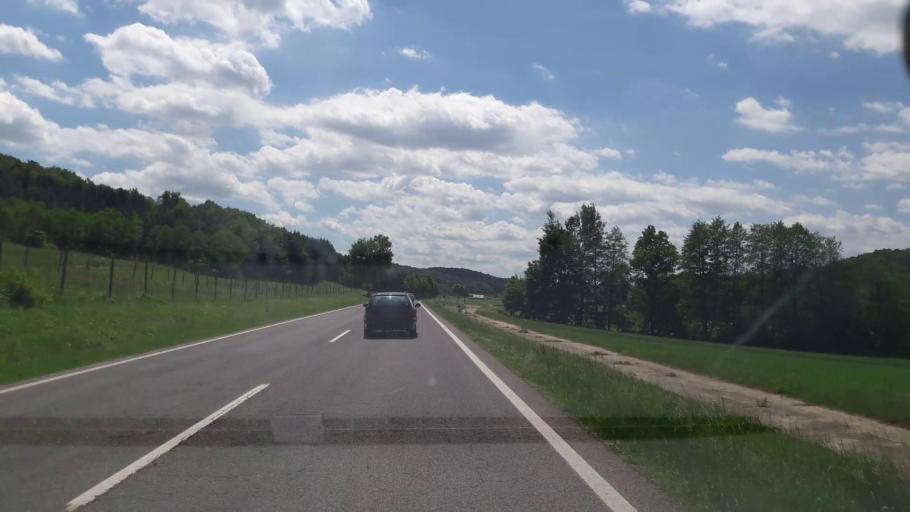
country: AT
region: Burgenland
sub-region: Politischer Bezirk Jennersdorf
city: Sankt Martin an der Raab
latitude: 46.9002
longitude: 16.1020
